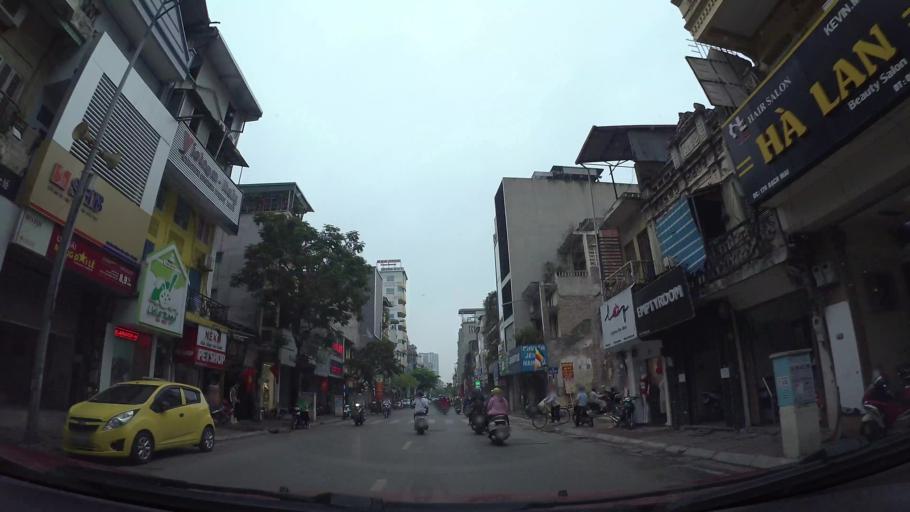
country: VN
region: Ha Noi
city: Hai BaTrung
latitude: 21.0051
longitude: 105.8512
